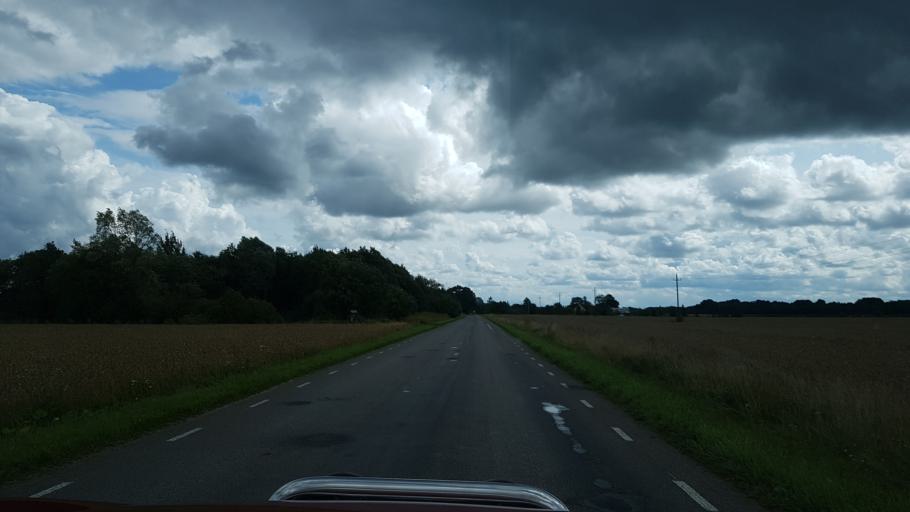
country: EE
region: Laeaene
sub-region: Lihula vald
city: Lihula
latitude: 58.7143
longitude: 24.0001
